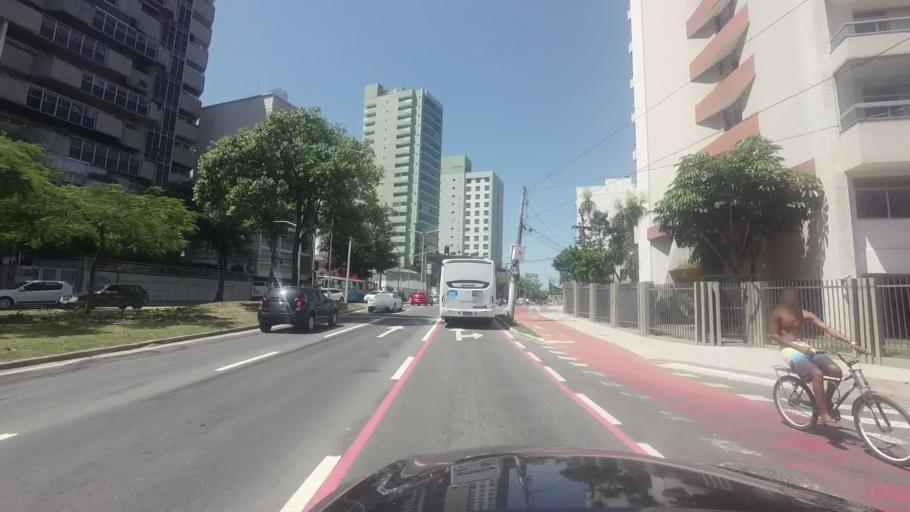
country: BR
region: Espirito Santo
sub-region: Vila Velha
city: Vila Velha
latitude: -20.2980
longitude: -40.2916
